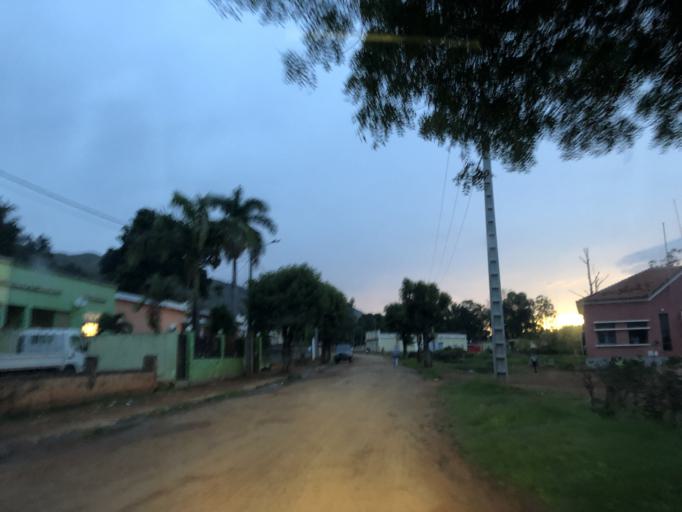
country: AO
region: Cuanza Sul
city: Uacu Cungo
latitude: -11.3637
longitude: 15.1158
